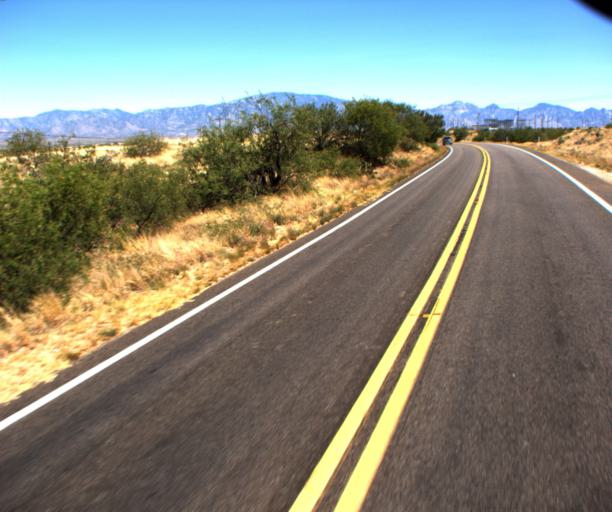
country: US
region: Arizona
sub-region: Pima County
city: Catalina
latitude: 32.6071
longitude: -110.9860
